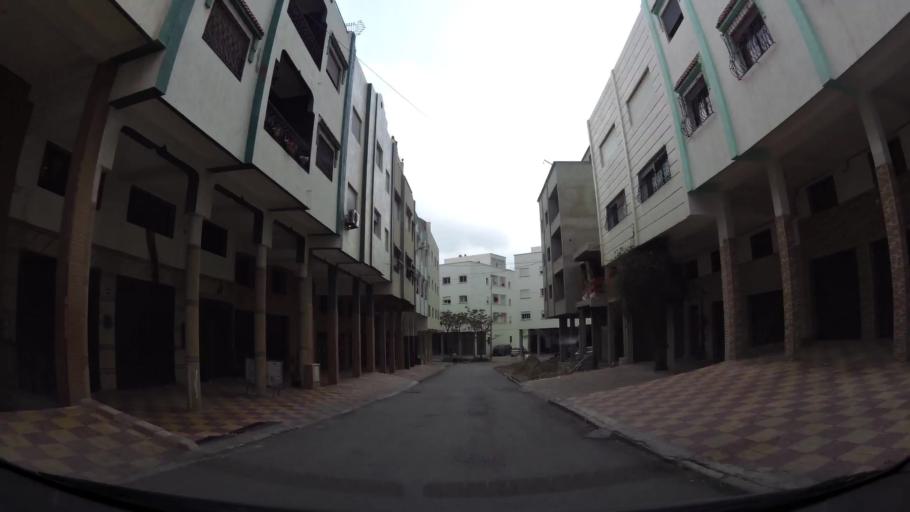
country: MA
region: Tanger-Tetouan
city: Tetouan
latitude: 35.5626
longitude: -5.3600
